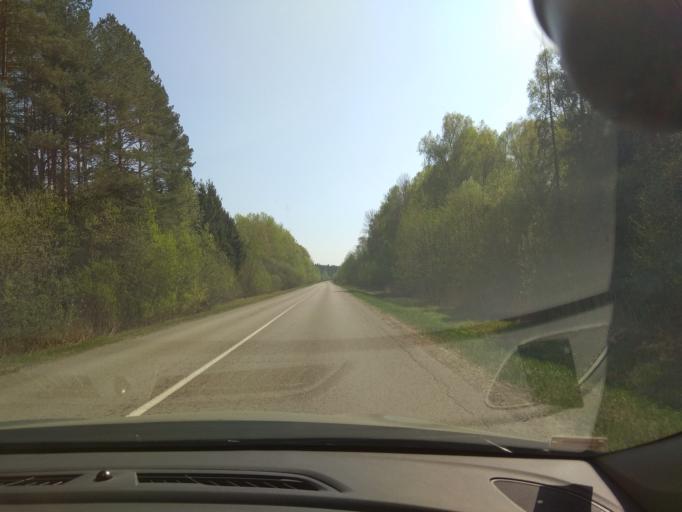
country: LT
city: Linkuva
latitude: 55.9951
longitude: 24.1713
